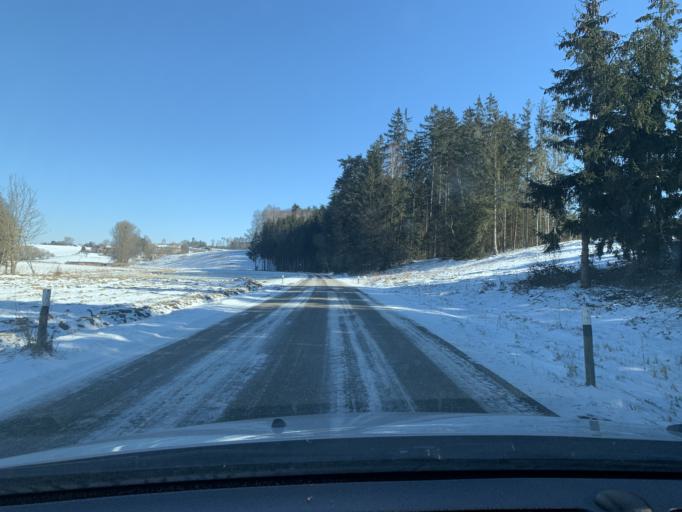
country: DE
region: Bavaria
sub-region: Upper Bavaria
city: Lohkirchen
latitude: 48.3184
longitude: 12.4587
